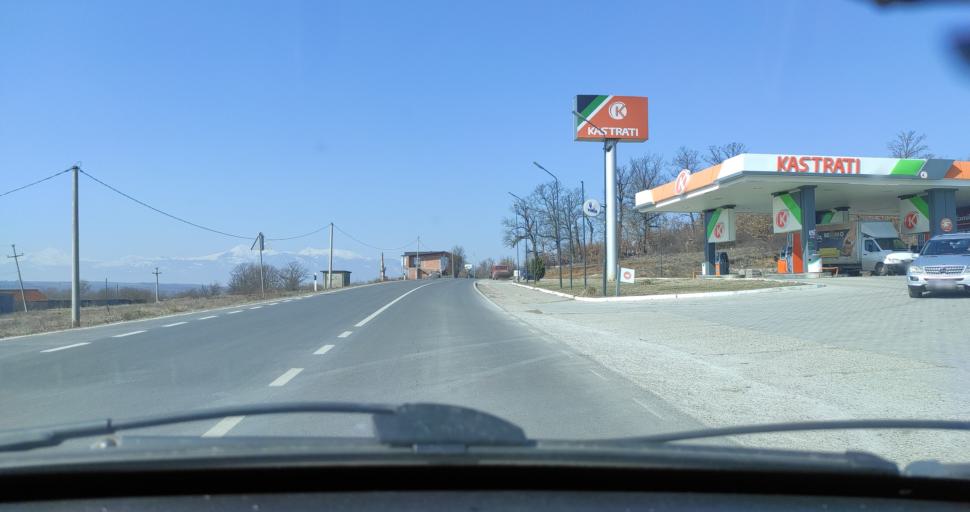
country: XK
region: Pec
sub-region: Komuna e Klines
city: Klina
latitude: 42.5905
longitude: 20.5556
